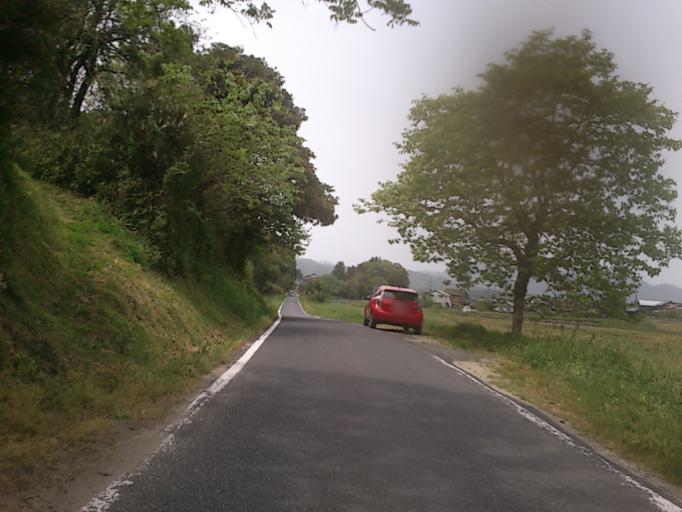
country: JP
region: Kyoto
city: Miyazu
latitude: 35.6039
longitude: 135.0978
